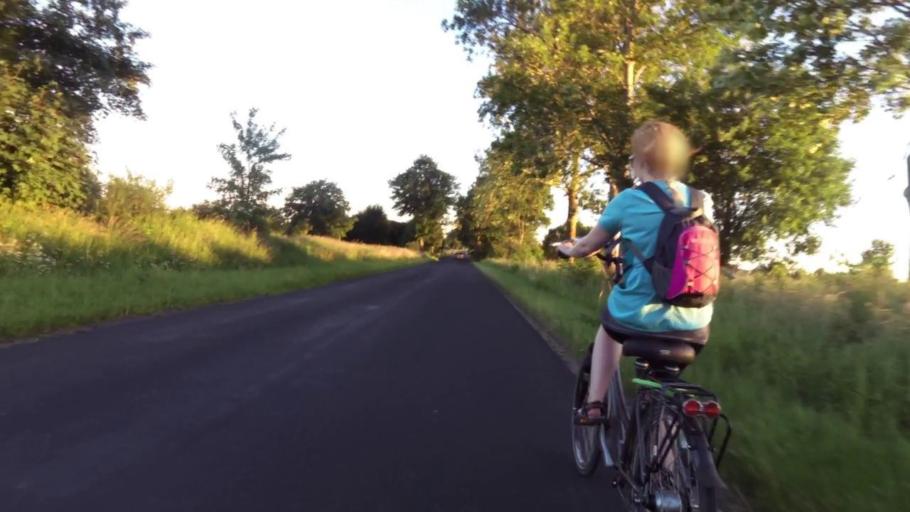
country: PL
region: West Pomeranian Voivodeship
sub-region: Powiat bialogardzki
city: Bialogard
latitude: 54.0210
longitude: 16.0122
